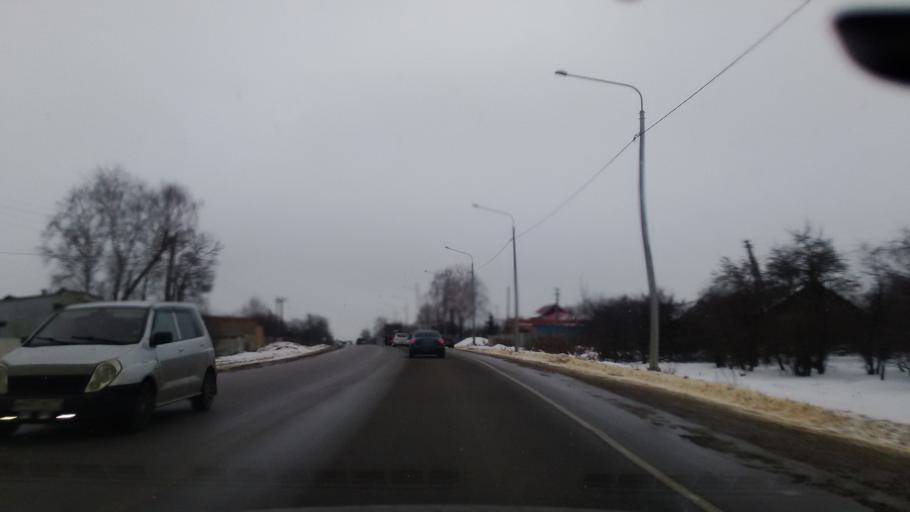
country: RU
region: Tula
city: Borodinskiy
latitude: 54.0236
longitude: 37.8944
